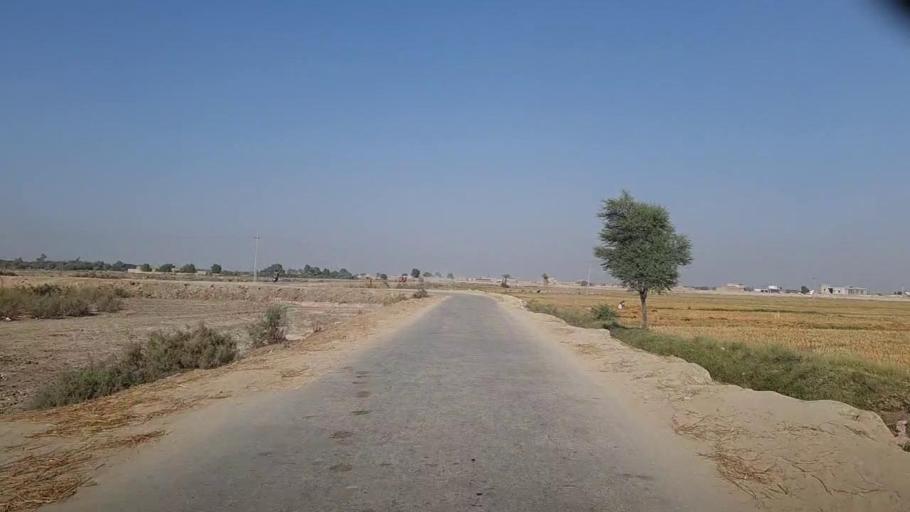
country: PK
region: Sindh
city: Tangwani
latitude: 28.2563
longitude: 68.9967
